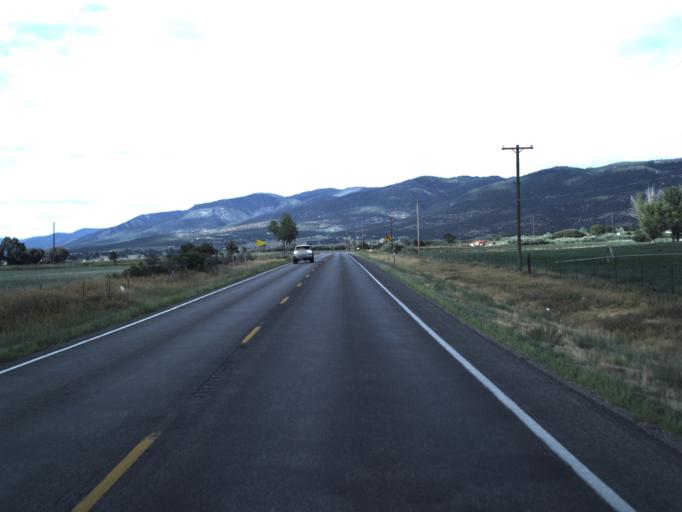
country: US
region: Utah
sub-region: Sanpete County
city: Fairview
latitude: 39.5920
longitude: -111.4479
